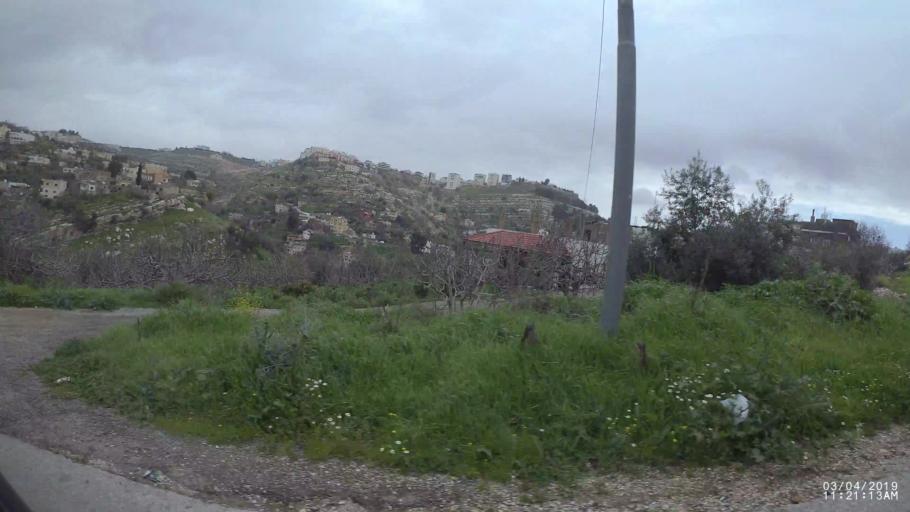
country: JO
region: Amman
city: Wadi as Sir
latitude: 31.9585
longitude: 35.8124
